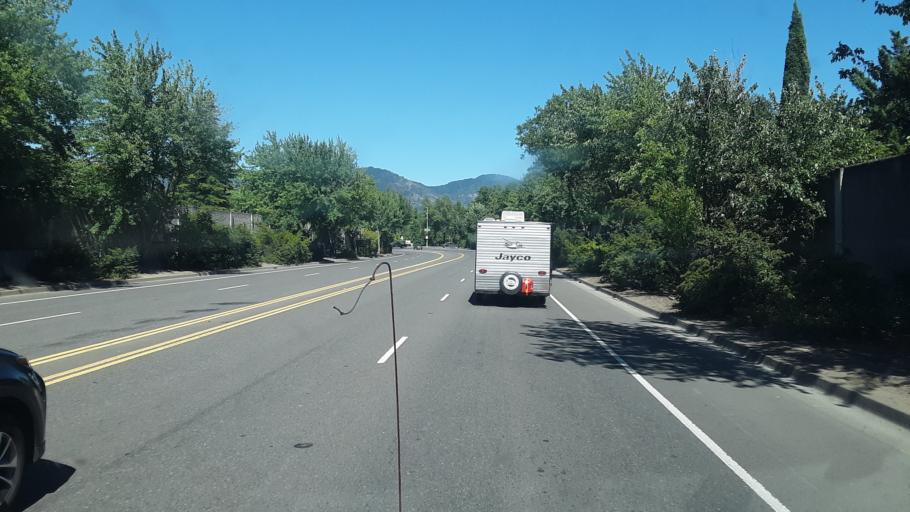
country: US
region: Oregon
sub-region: Josephine County
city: Grants Pass
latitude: 42.4264
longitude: -123.3228
